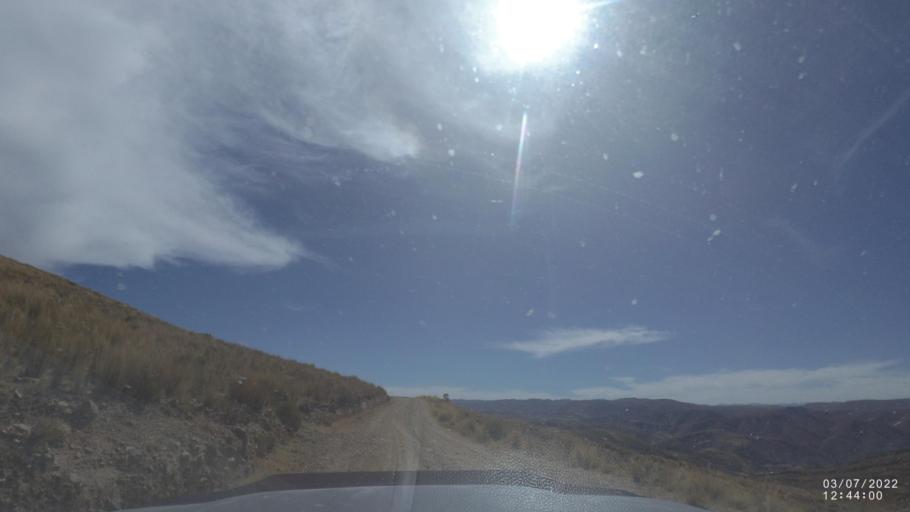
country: BO
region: Cochabamba
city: Irpa Irpa
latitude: -17.7812
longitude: -66.6314
